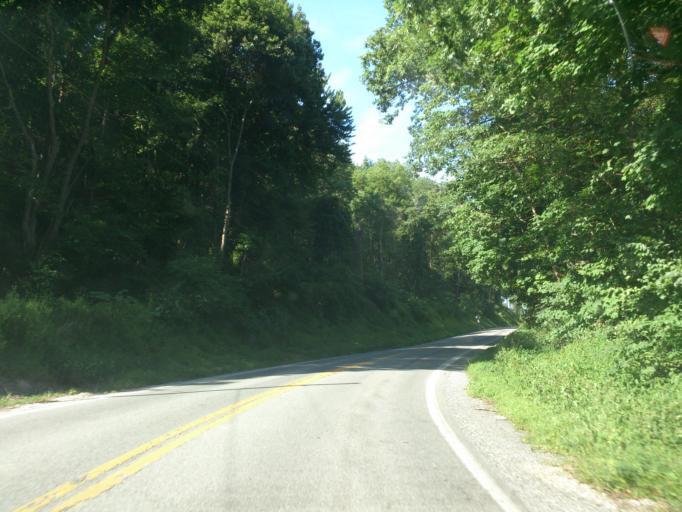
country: US
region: Pennsylvania
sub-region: York County
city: Susquehanna Trails
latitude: 39.8097
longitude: -76.4734
